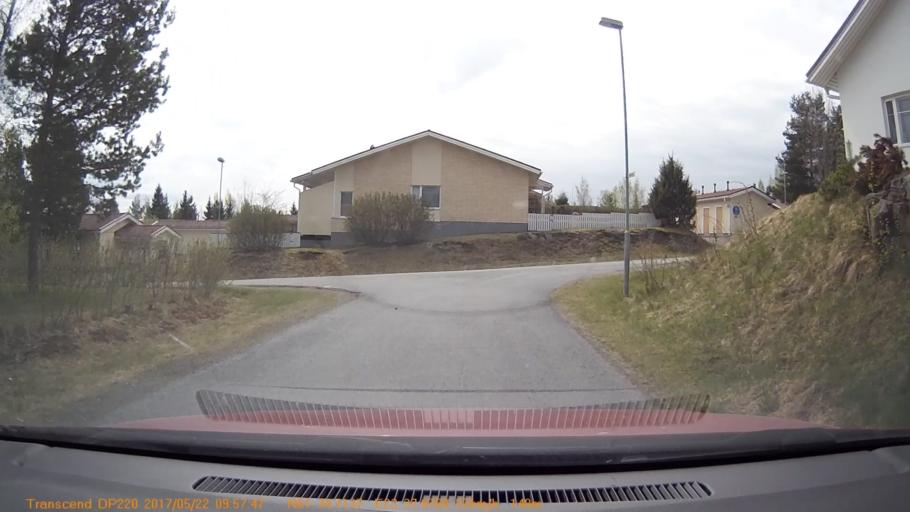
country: FI
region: Pirkanmaa
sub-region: Tampere
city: Yloejaervi
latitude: 61.5785
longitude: 23.6313
